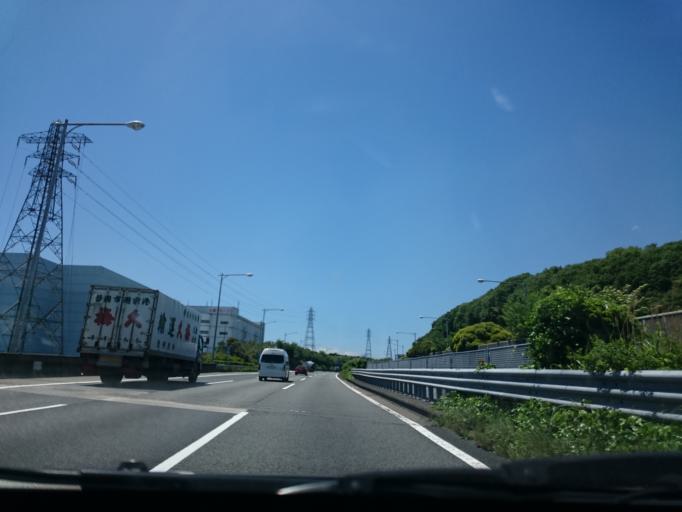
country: JP
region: Kanagawa
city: Hadano
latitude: 35.3518
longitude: 139.2337
